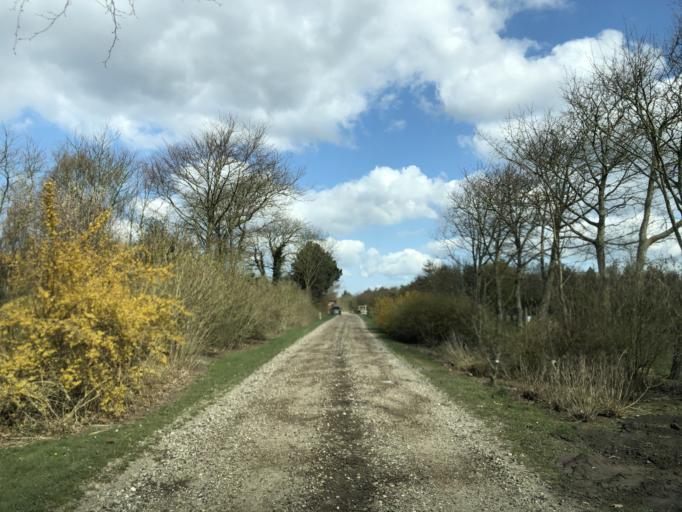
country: DK
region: Central Jutland
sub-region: Holstebro Kommune
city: Ulfborg
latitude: 56.3812
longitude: 8.2096
